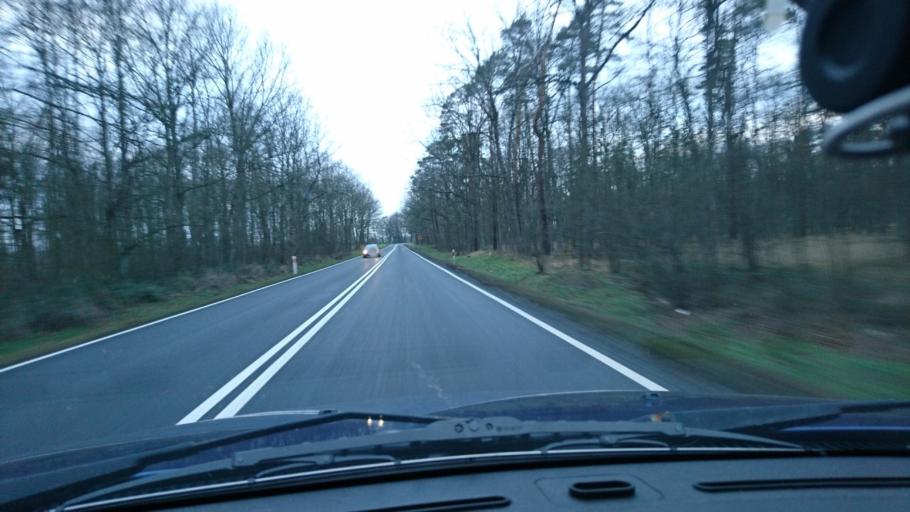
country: PL
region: Opole Voivodeship
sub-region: Powiat kluczborski
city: Byczyna
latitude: 51.1466
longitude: 18.1898
